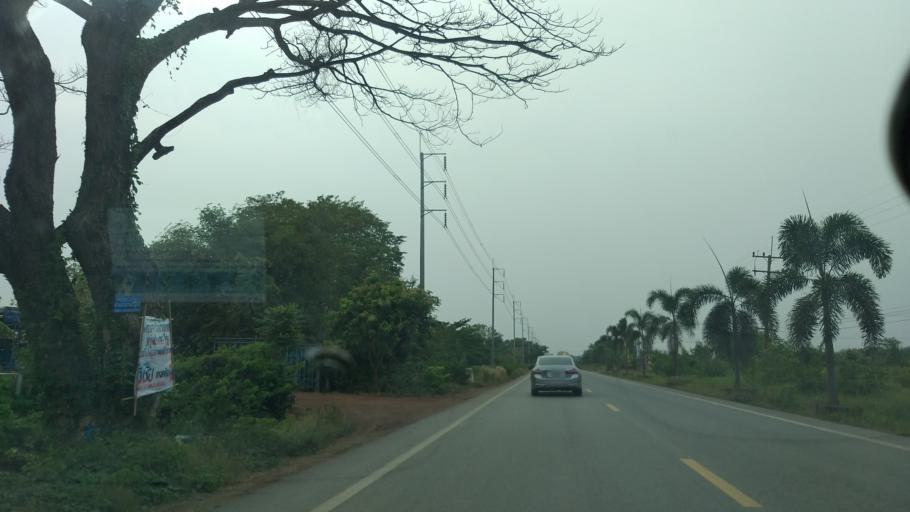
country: TH
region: Chachoengsao
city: Plaeng Yao
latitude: 13.5863
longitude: 101.2154
